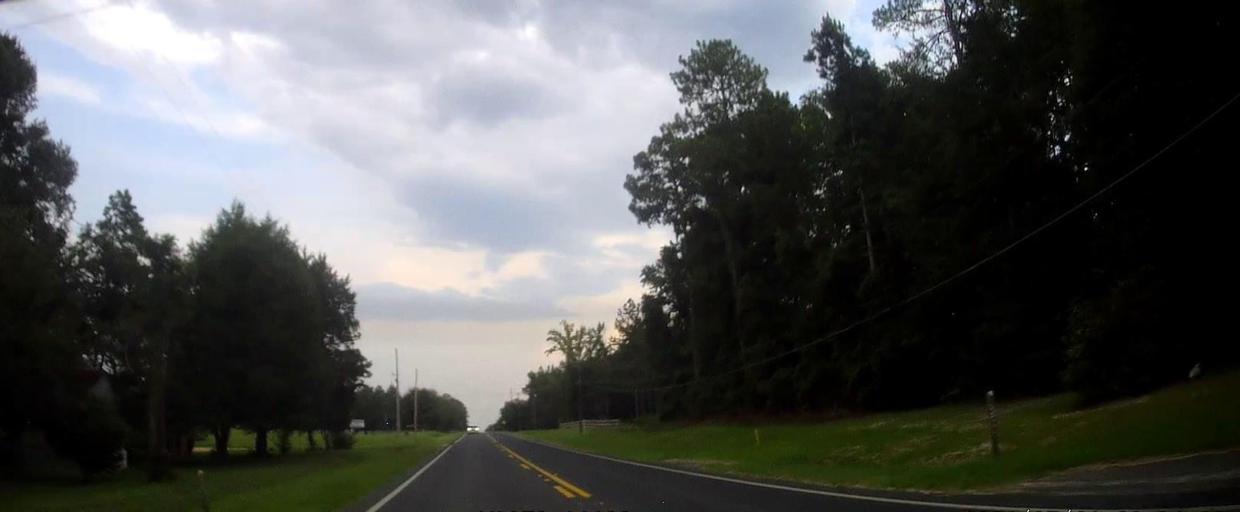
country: US
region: Georgia
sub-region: Laurens County
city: East Dublin
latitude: 32.5381
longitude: -82.8510
